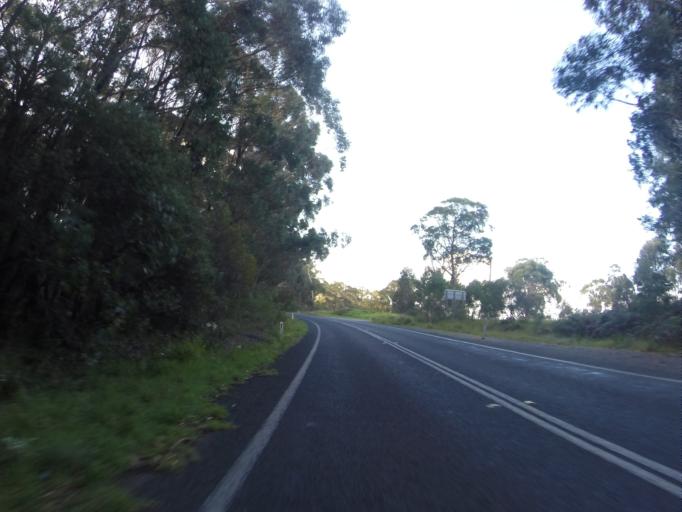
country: AU
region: New South Wales
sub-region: Shoalhaven Shire
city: Kangaroo Valley
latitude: -34.6566
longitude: 150.4900
